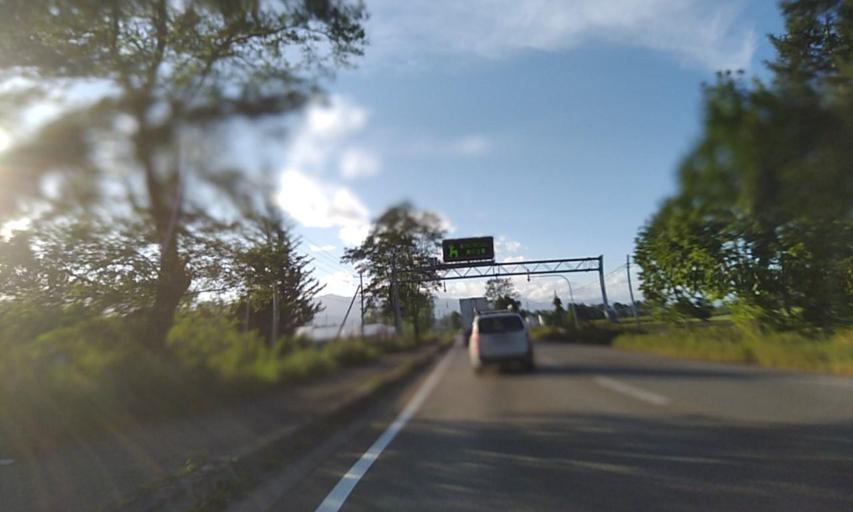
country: JP
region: Hokkaido
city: Otofuke
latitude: 42.9414
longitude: 142.9529
